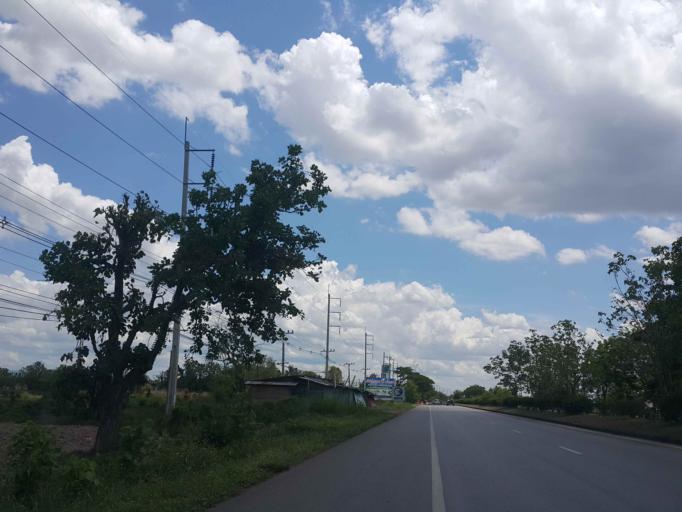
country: TH
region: Phrae
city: Nong Muang Khai
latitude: 18.2553
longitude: 100.2310
